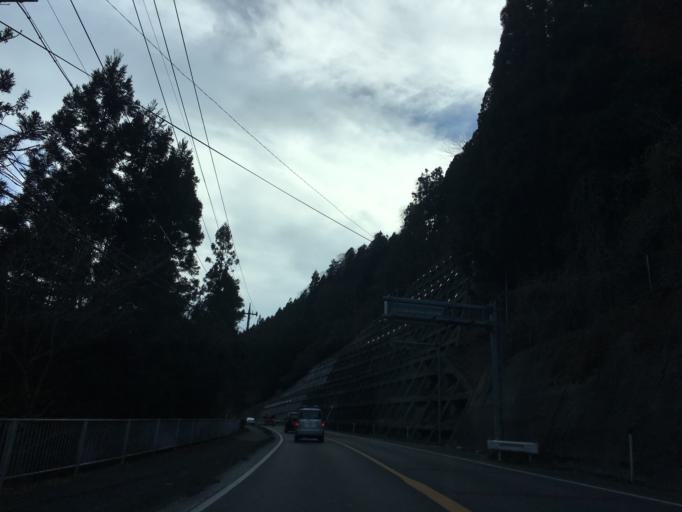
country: JP
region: Saitama
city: Chichibu
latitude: 35.9685
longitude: 139.1613
